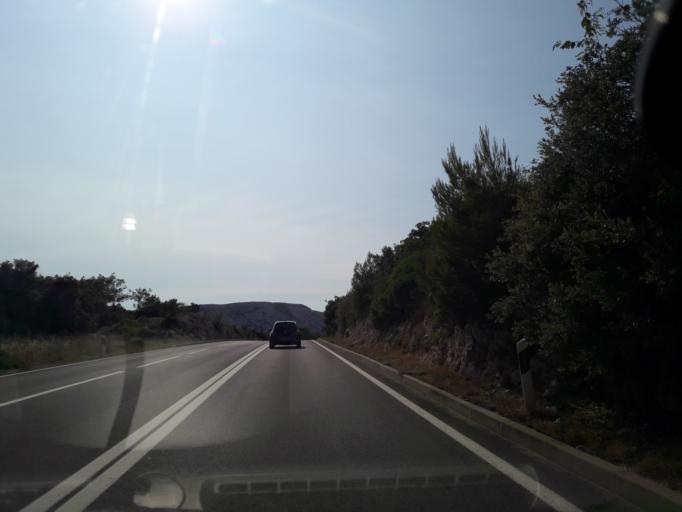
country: HR
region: Primorsko-Goranska
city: Banjol
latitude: 44.7062
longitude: 14.8400
